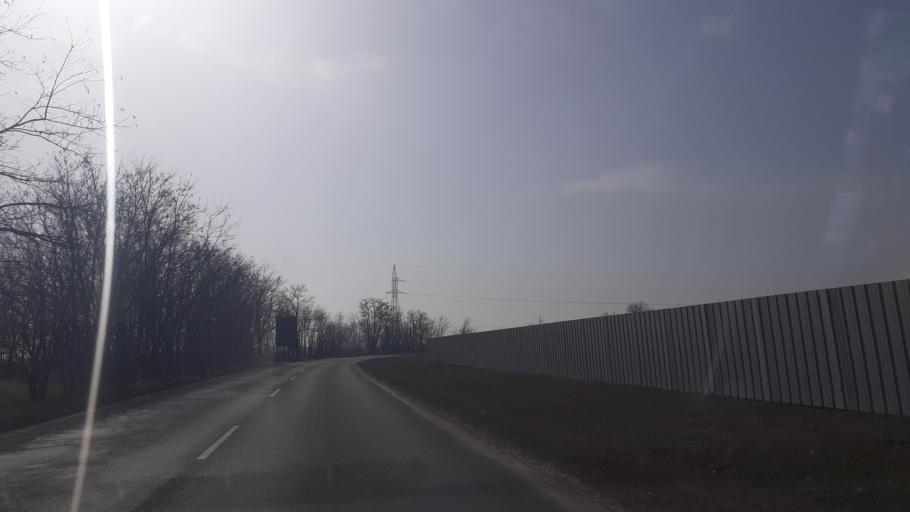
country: HU
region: Pest
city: Orkeny
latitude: 47.1458
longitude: 19.4602
